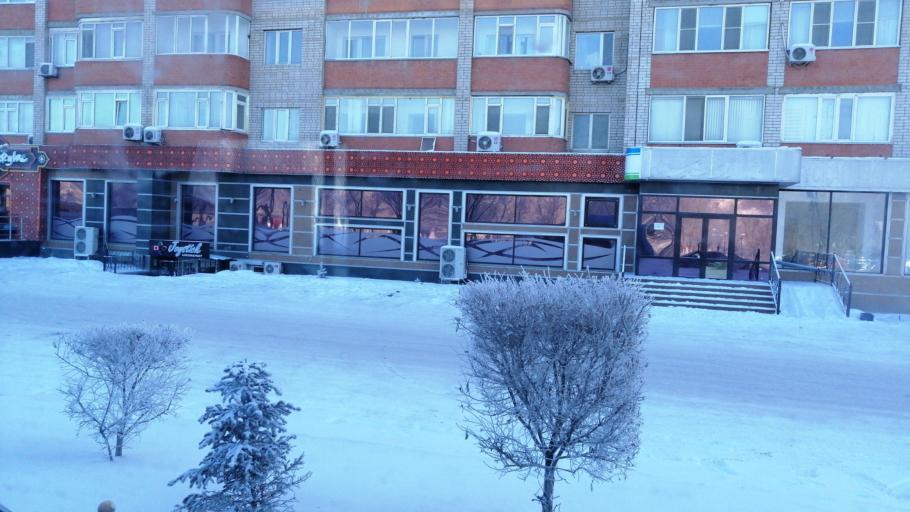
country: KZ
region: Aqtoebe
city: Aqtobe
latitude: 50.2920
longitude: 57.1680
